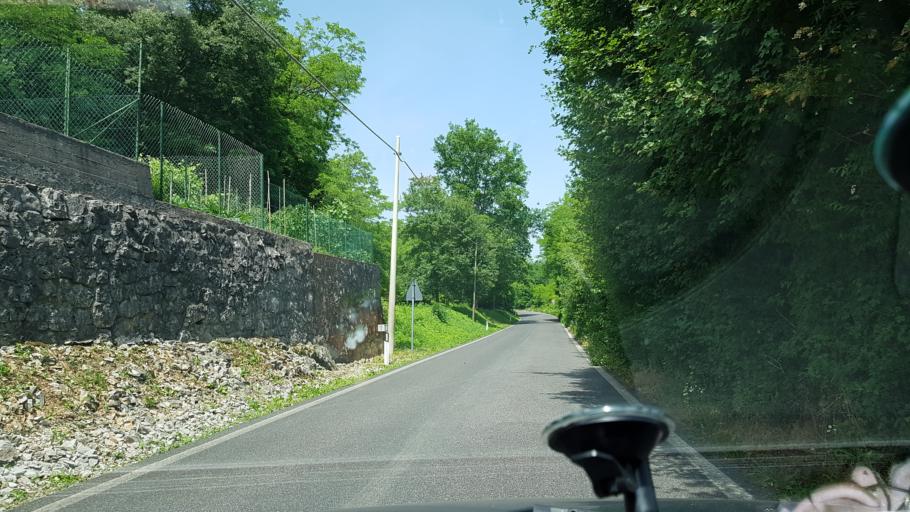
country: IT
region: Friuli Venezia Giulia
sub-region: Provincia di Gorizia
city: Savogna d'Isonzo
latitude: 45.8880
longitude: 13.5782
